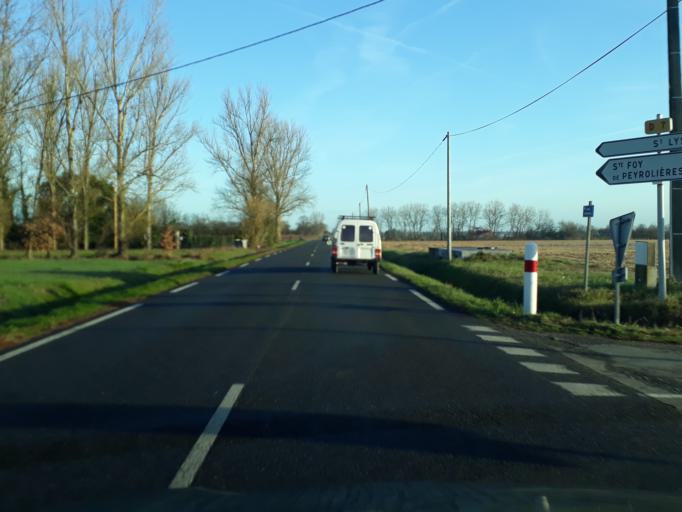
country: FR
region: Midi-Pyrenees
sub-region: Departement de la Haute-Garonne
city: Rieumes
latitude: 43.4434
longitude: 1.1362
